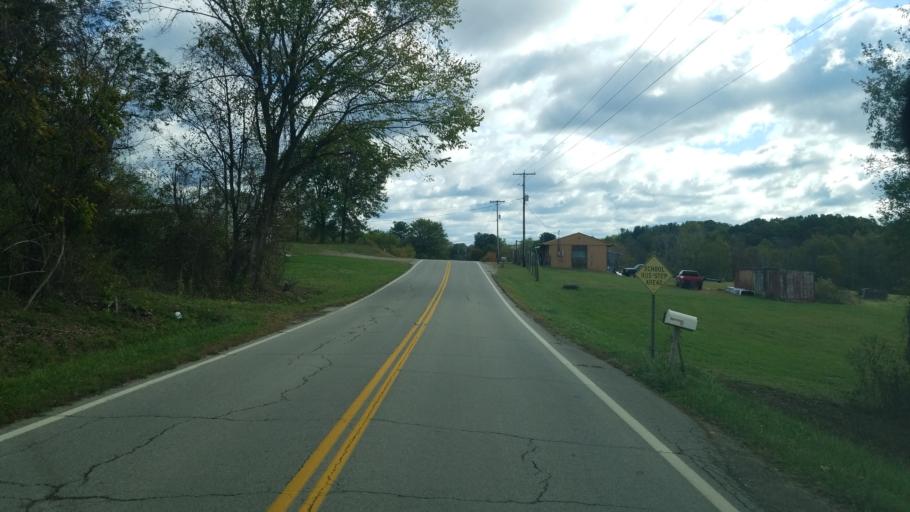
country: US
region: Ohio
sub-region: Jackson County
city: Wellston
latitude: 39.1617
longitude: -82.4657
